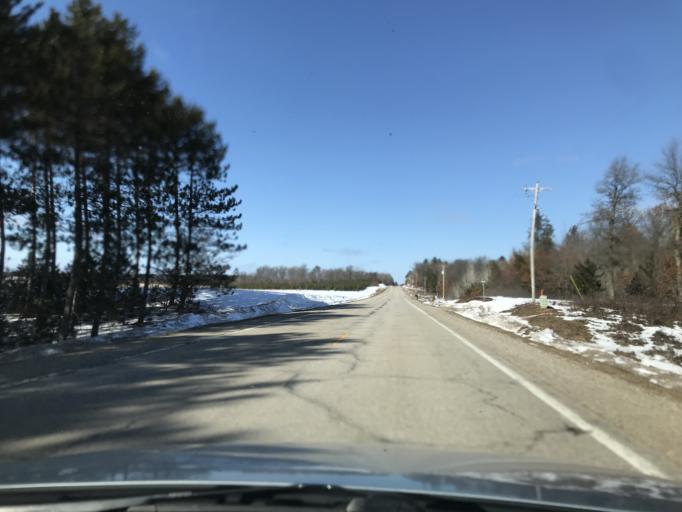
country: US
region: Wisconsin
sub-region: Marinette County
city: Niagara
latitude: 45.3471
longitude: -88.1013
